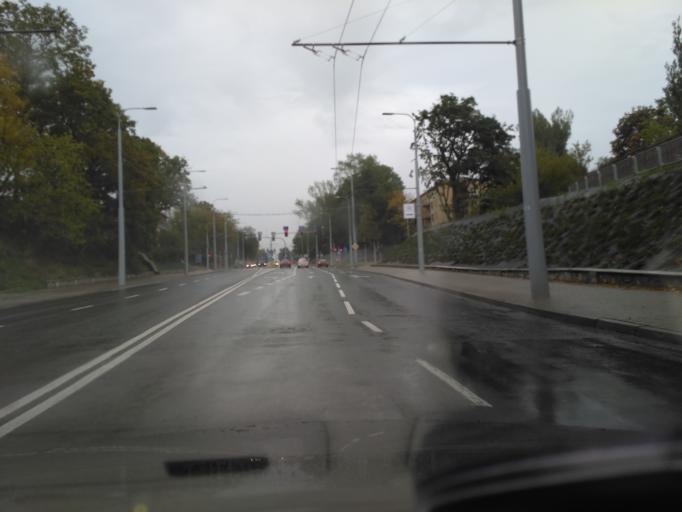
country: PL
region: Lublin Voivodeship
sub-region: Powiat lubelski
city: Lublin
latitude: 51.2352
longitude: 22.5804
